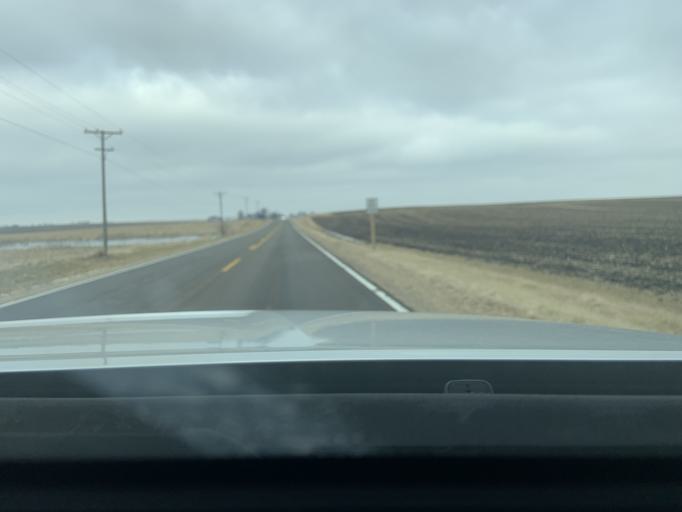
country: US
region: Illinois
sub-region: LaSalle County
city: Seneca
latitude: 41.4031
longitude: -88.6140
